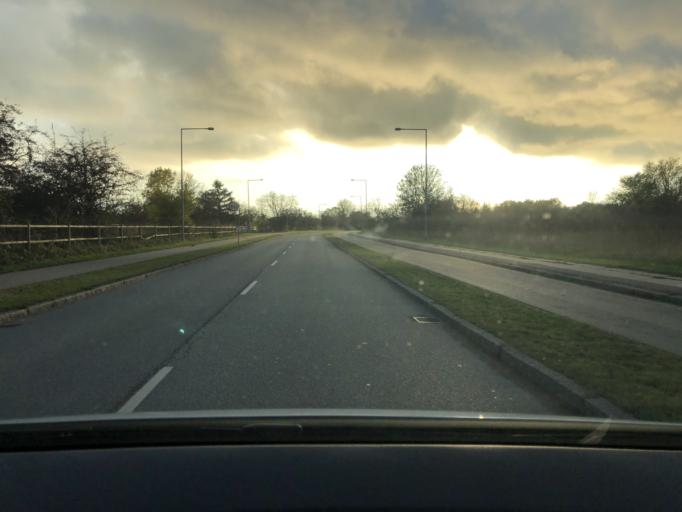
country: DK
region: Capital Region
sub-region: Tarnby Kommune
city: Tarnby
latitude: 55.6093
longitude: 12.6079
